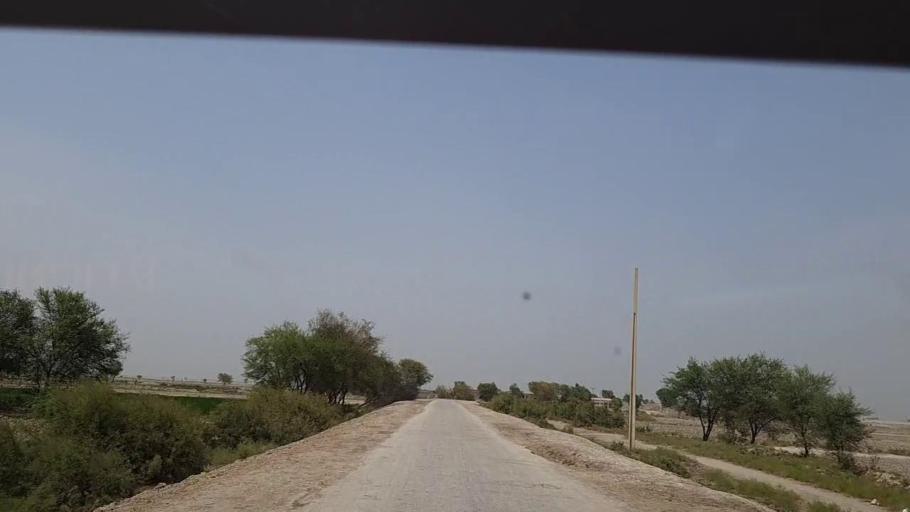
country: PK
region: Sindh
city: Khairpur Nathan Shah
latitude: 27.0507
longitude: 67.6433
